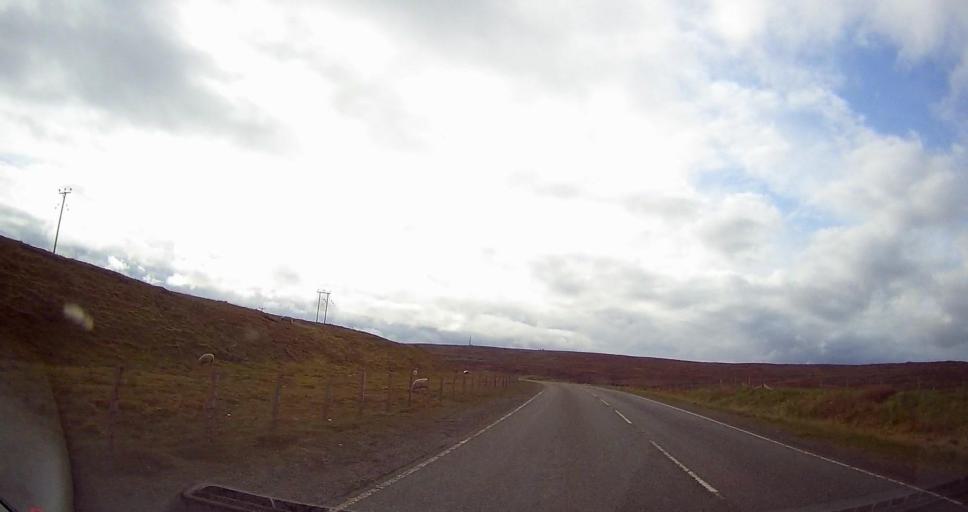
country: GB
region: Scotland
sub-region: Shetland Islands
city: Lerwick
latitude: 60.4423
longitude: -1.2325
